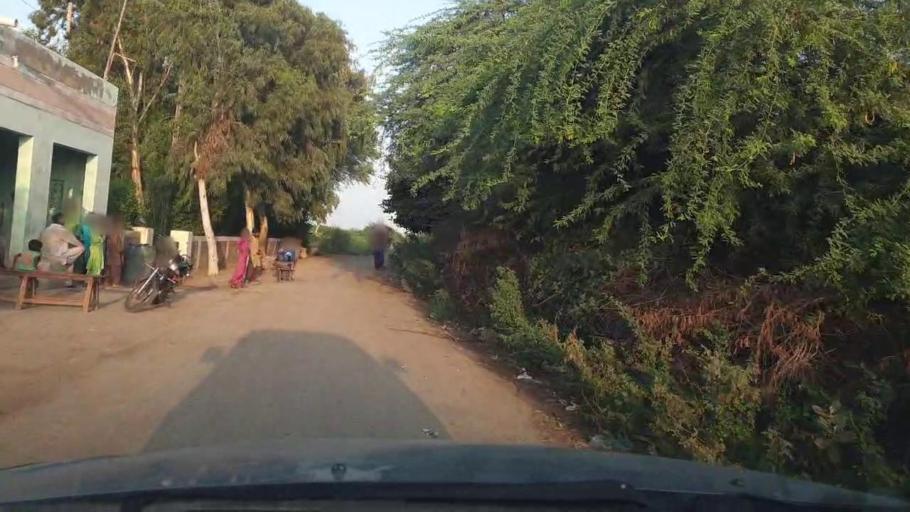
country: PK
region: Sindh
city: Tando Ghulam Ali
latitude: 25.1587
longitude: 68.9718
